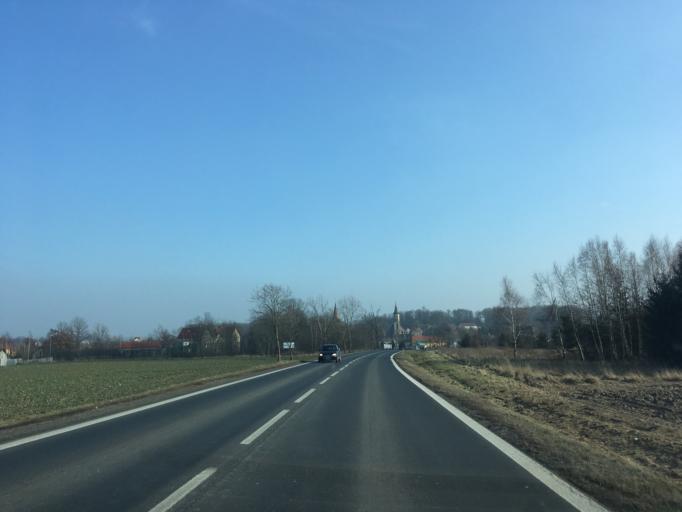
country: PL
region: Lower Silesian Voivodeship
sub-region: Powiat boleslawiecki
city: Boleslawiec
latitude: 51.2607
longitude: 15.6746
